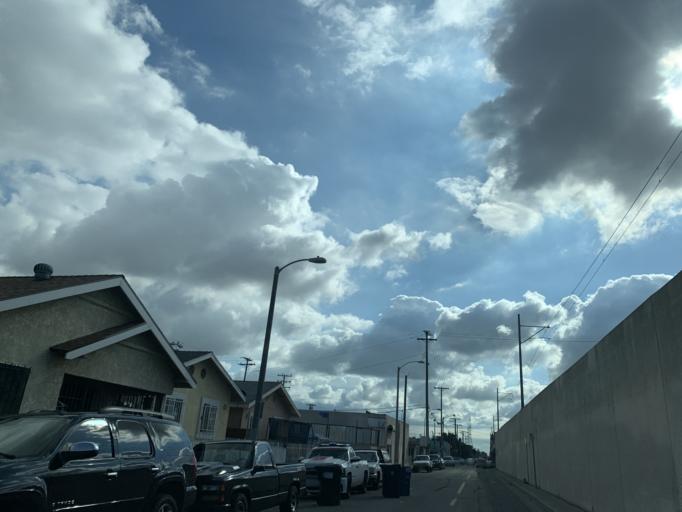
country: US
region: California
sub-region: Los Angeles County
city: Florence-Graham
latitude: 33.9614
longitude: -118.2431
